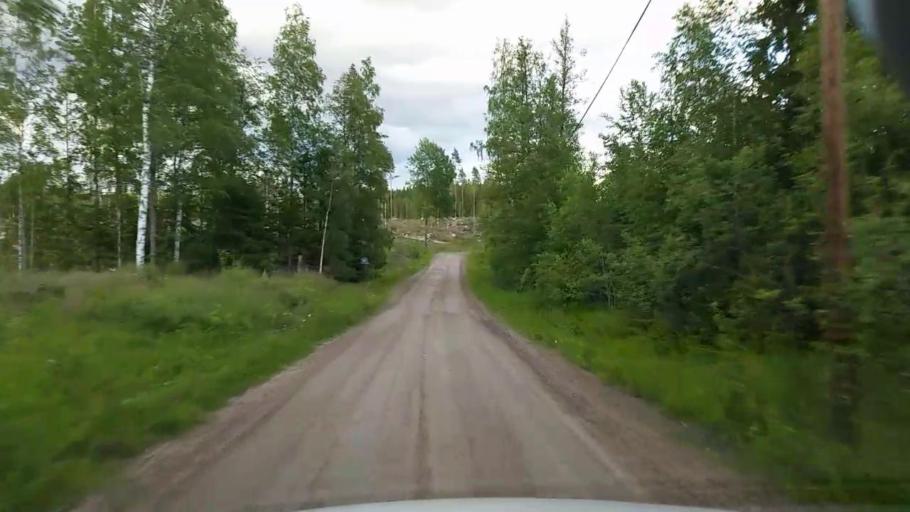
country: SE
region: Vaestmanland
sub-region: Kopings Kommun
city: Kolsva
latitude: 59.7763
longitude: 15.8725
